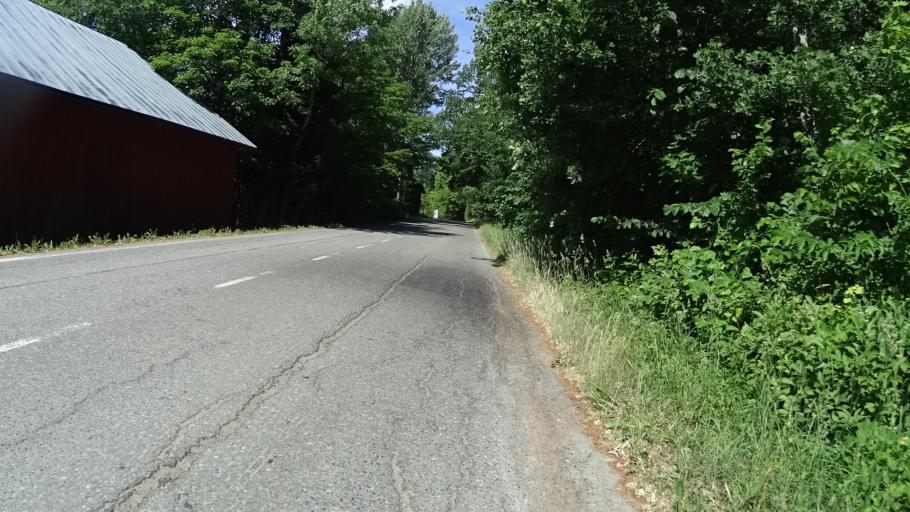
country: FI
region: Uusimaa
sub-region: Raaseporin
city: Karis
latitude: 60.0895
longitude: 23.6363
